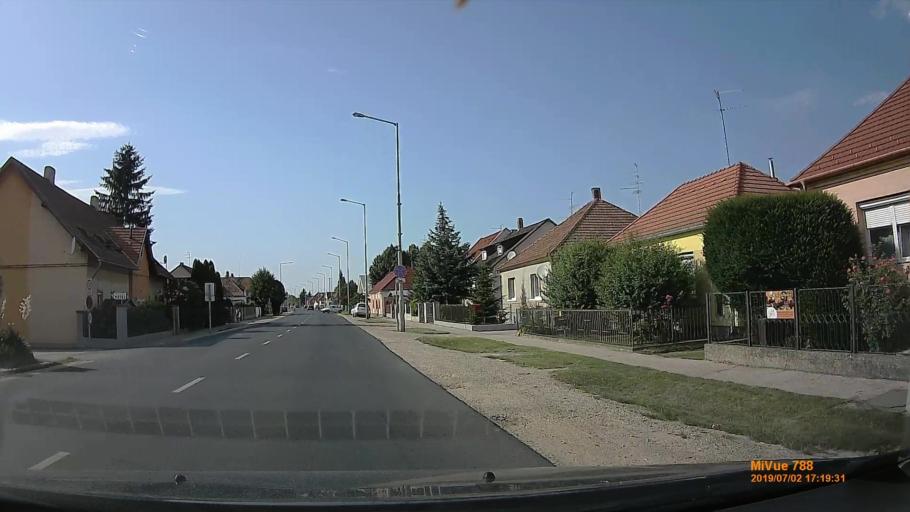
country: HU
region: Gyor-Moson-Sopron
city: Mosonmagyarovar
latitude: 47.8838
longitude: 17.2719
